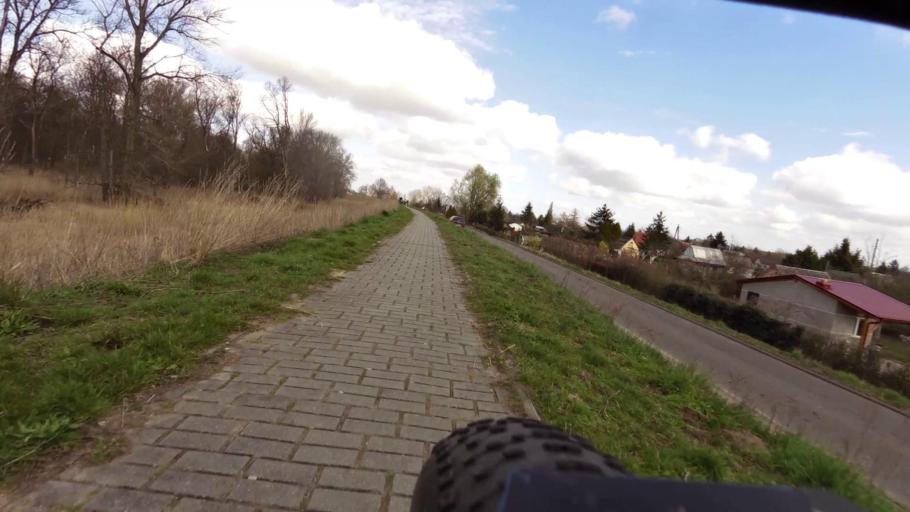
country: PL
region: Lubusz
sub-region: Powiat slubicki
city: Slubice
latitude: 52.3672
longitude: 14.5626
